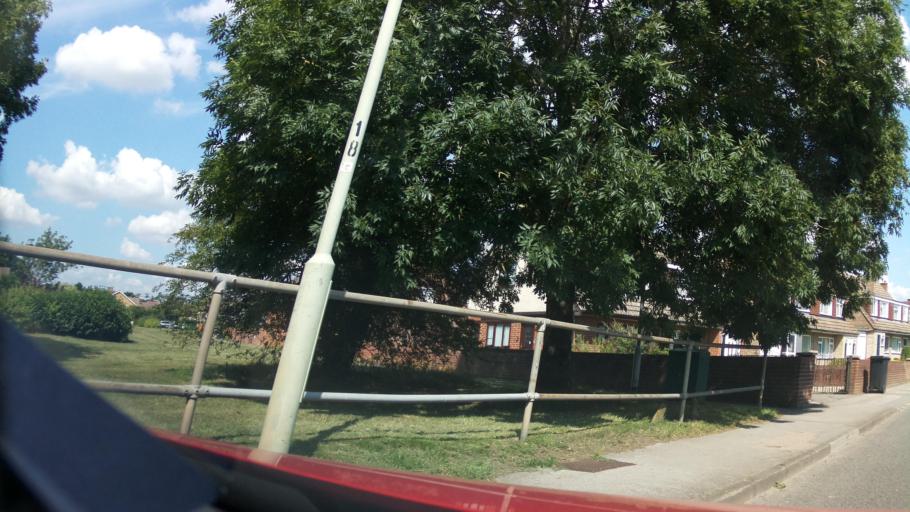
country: GB
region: England
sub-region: West Berkshire
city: Thatcham
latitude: 51.4017
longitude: -1.2727
